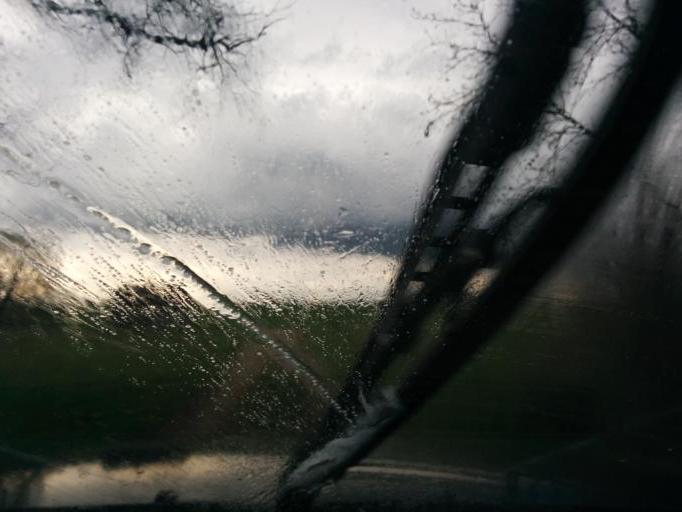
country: LV
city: Tervete
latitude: 56.3722
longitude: 23.5139
